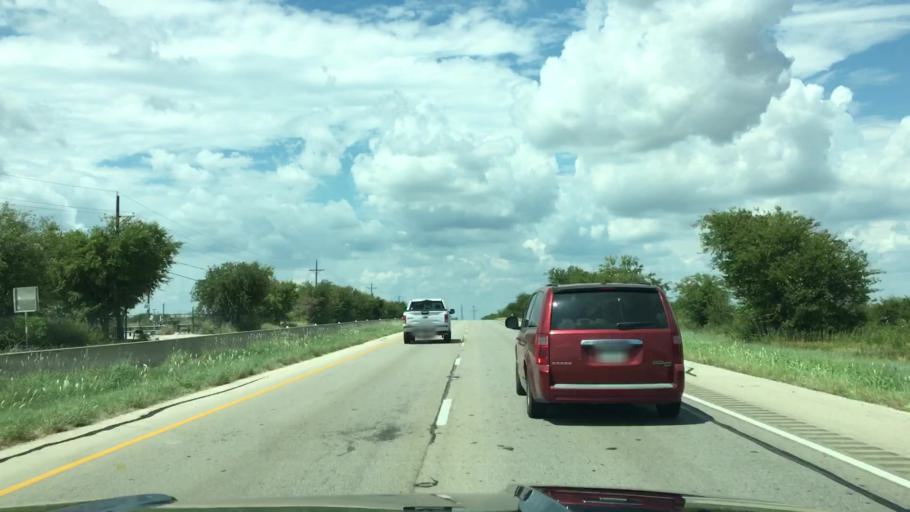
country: US
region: Texas
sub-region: Tarrant County
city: Saginaw
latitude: 32.8925
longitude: -97.3917
